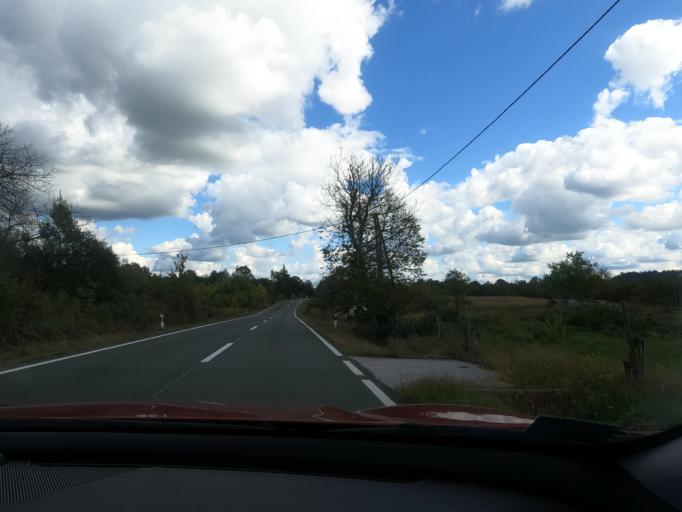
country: HR
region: Sisacko-Moslavacka
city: Glina
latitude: 45.3348
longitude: 15.9872
